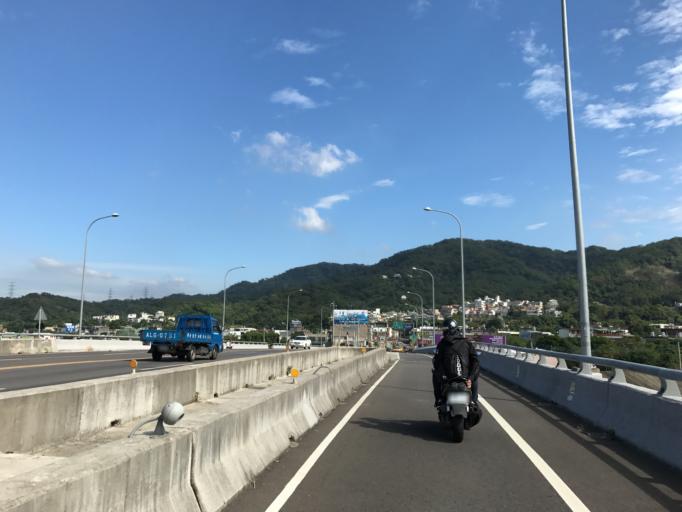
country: TW
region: Taiwan
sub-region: Hsinchu
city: Zhubei
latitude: 24.7482
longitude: 121.0944
